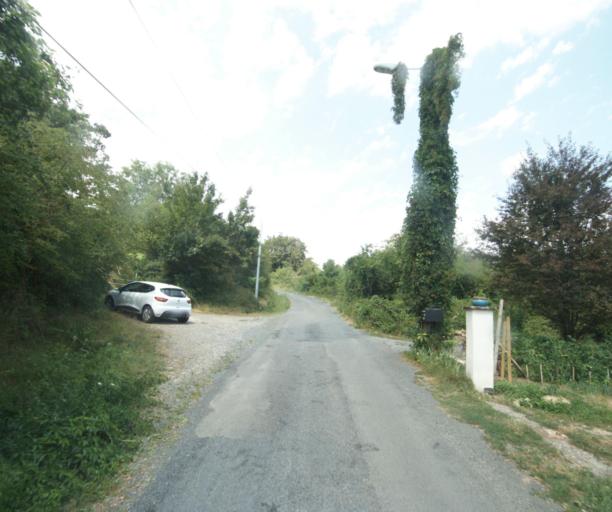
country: FR
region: Rhone-Alpes
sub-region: Departement du Rhone
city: Saint-Germain-Nuelles
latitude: 45.8434
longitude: 4.5995
